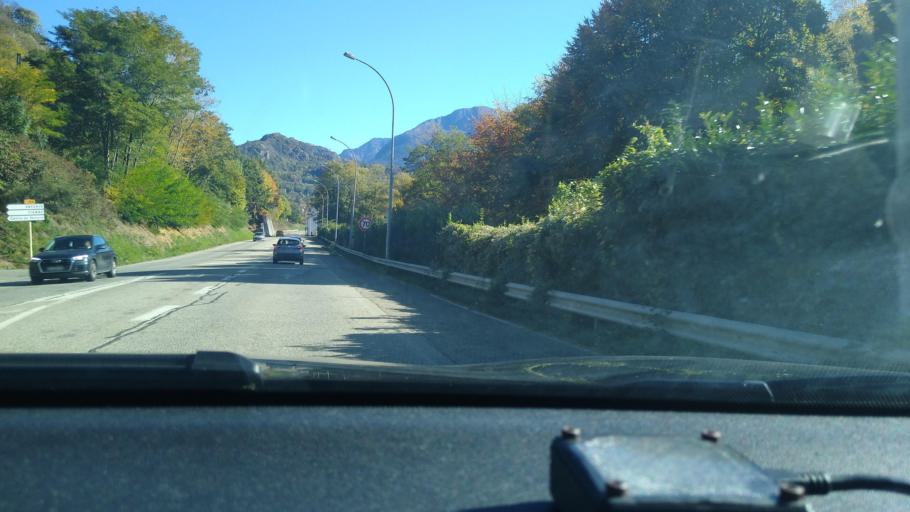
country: FR
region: Midi-Pyrenees
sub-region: Departement de l'Ariege
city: Ax-les-Thermes
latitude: 42.7287
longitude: 1.8261
